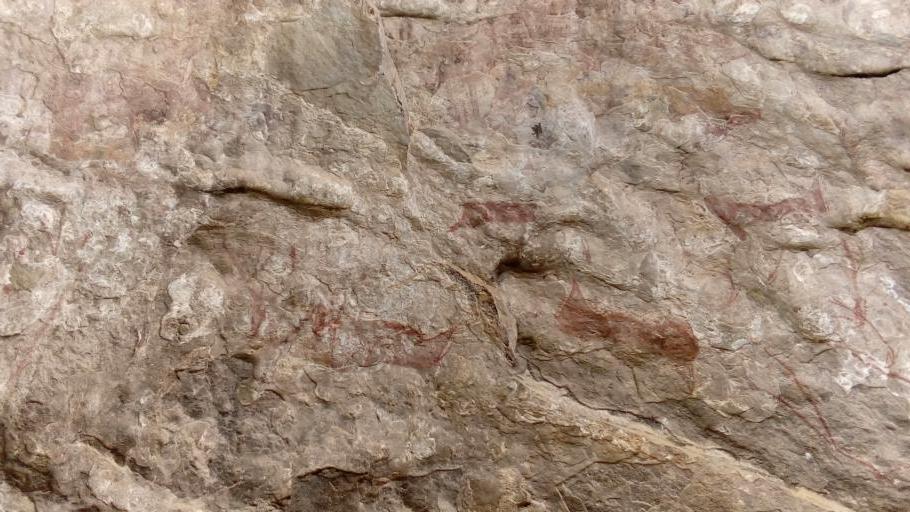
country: LS
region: Butha-Buthe
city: Butha-Buthe
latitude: -28.7542
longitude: 28.4944
